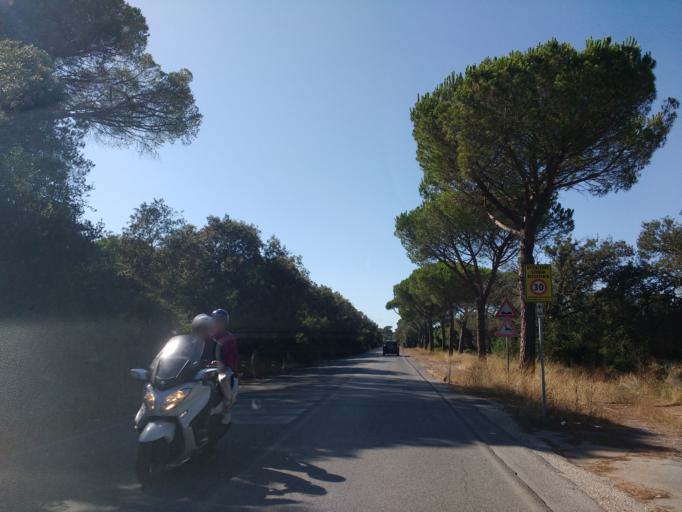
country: IT
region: Latium
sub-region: Citta metropolitana di Roma Capitale
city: Acilia-Castel Fusano-Ostia Antica
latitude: 41.7157
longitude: 12.3539
